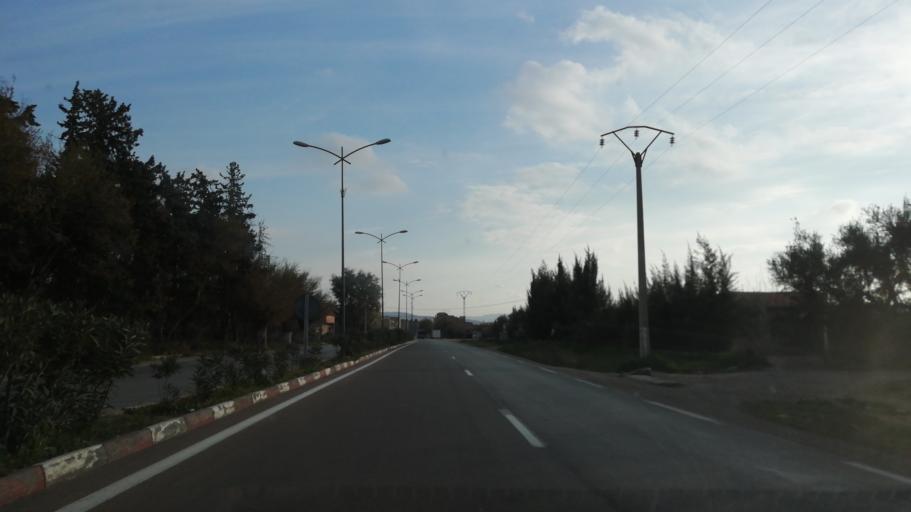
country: DZ
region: Mascara
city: Mascara
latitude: 35.6012
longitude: 0.0637
